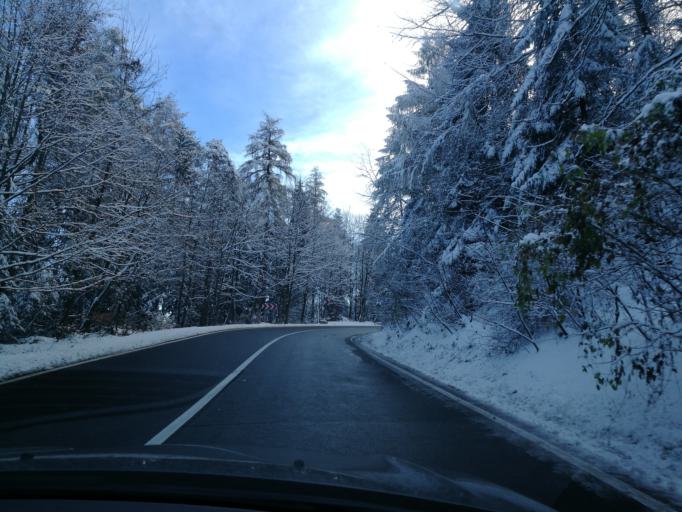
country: RO
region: Brasov
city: Brasov
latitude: 45.6298
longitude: 25.5573
